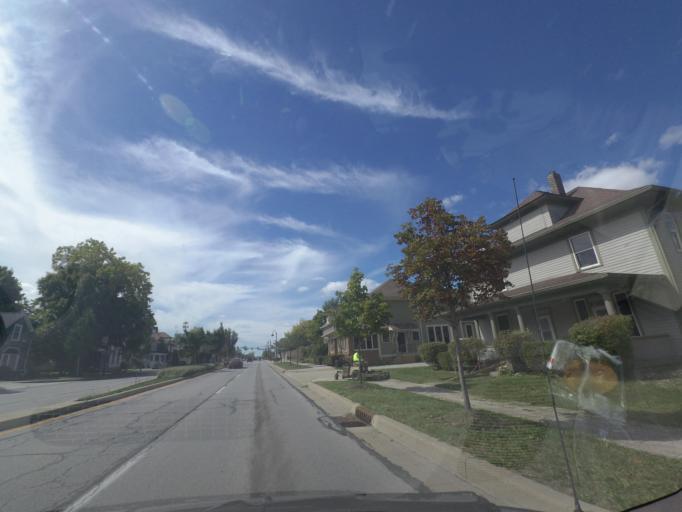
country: US
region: Indiana
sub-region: Marion County
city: Cumberland
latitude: 39.7766
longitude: -85.9551
